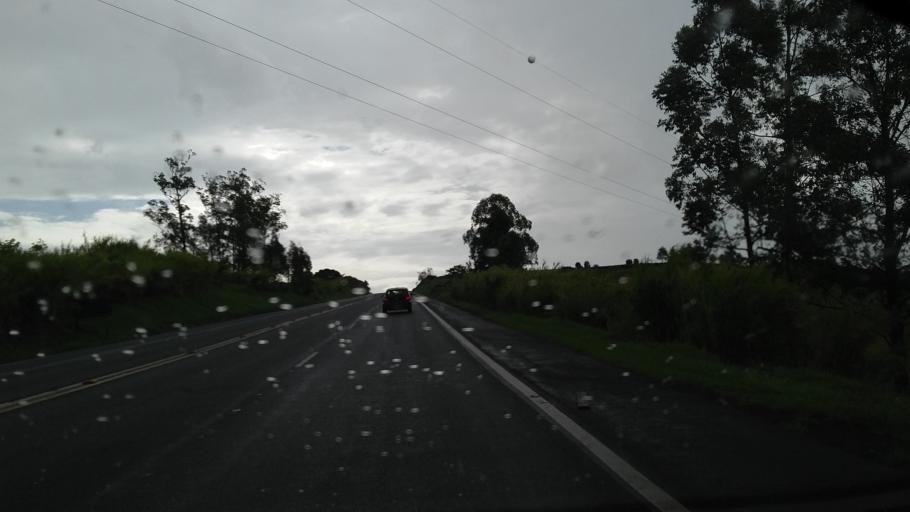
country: BR
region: Parana
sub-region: Mandaguari
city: Mandaguari
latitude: -23.4900
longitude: -51.6341
